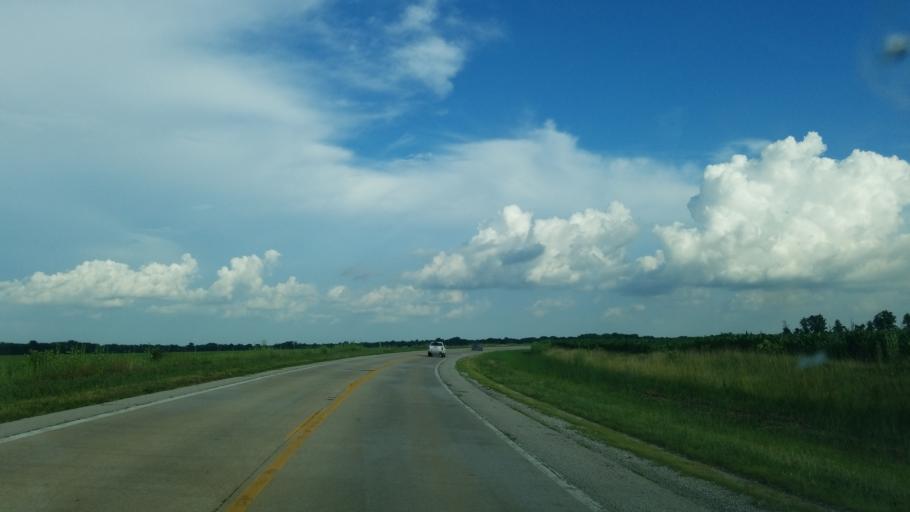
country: US
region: Illinois
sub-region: Marion County
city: Sandoval
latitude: 38.6031
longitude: -89.1101
